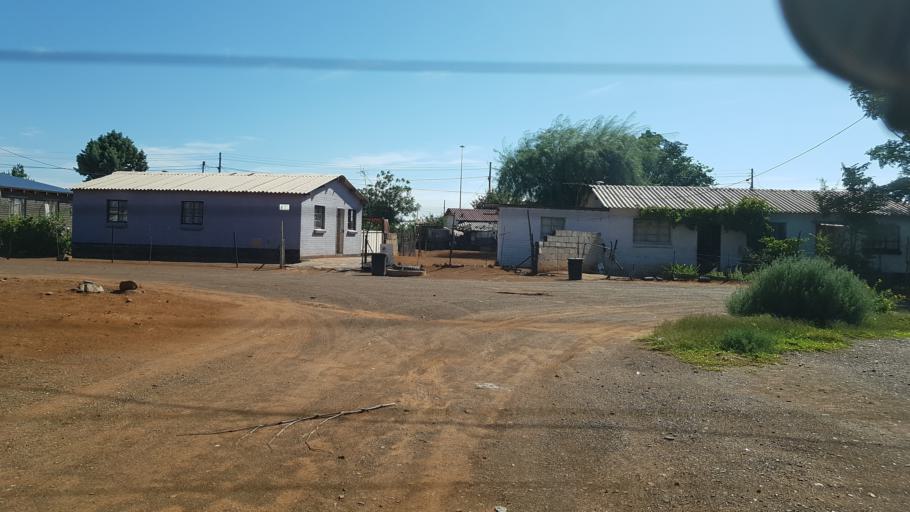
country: ZA
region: Northern Cape
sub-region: Siyanda District Municipality
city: Danielskuil
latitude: -28.1925
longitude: 23.5357
